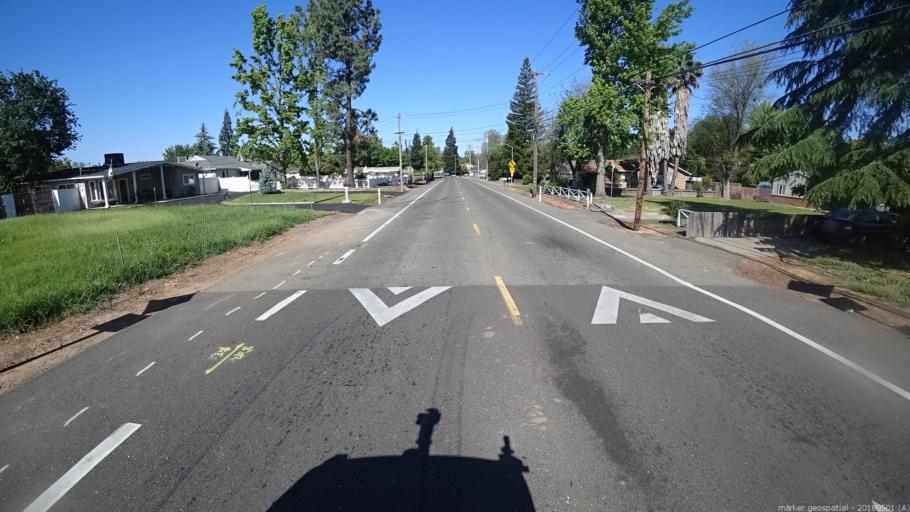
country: US
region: California
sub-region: Sacramento County
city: Arden-Arcade
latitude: 38.6344
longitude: -121.3740
